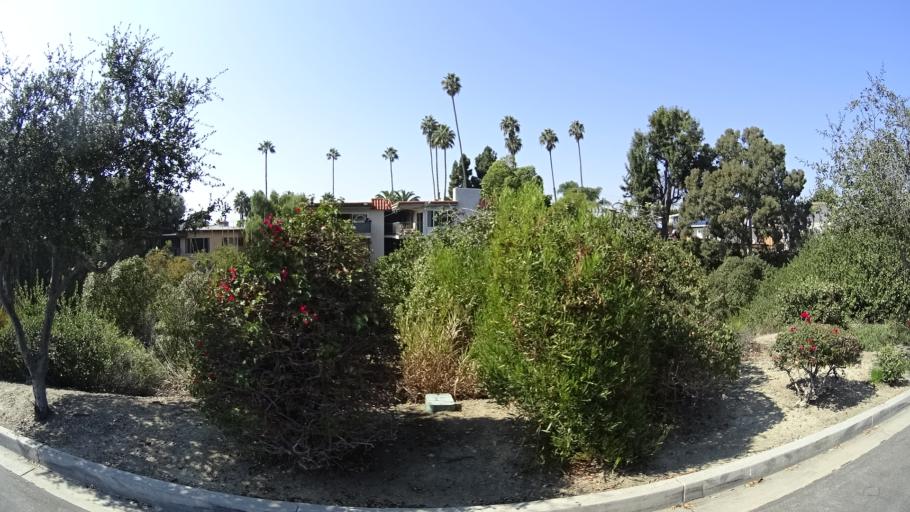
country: US
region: California
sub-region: Orange County
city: San Clemente
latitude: 33.4218
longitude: -117.6130
